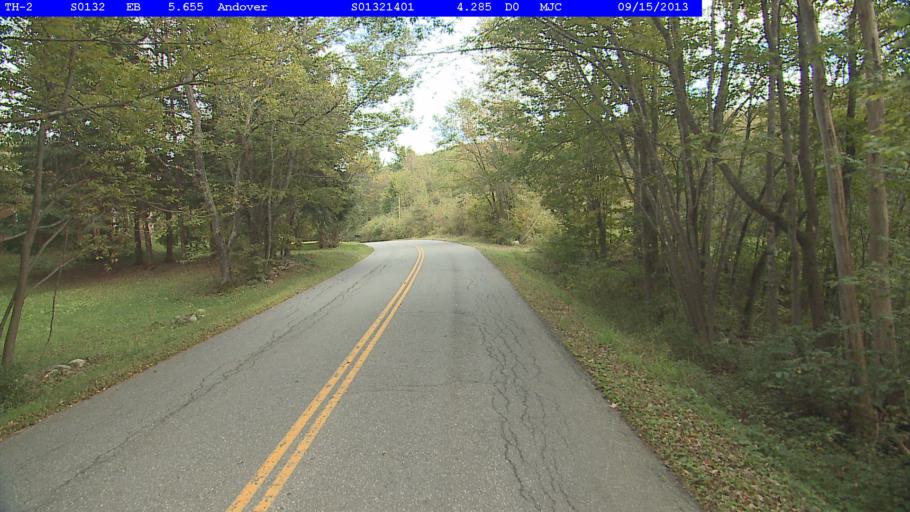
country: US
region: Vermont
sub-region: Windsor County
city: Chester
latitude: 43.2757
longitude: -72.6926
